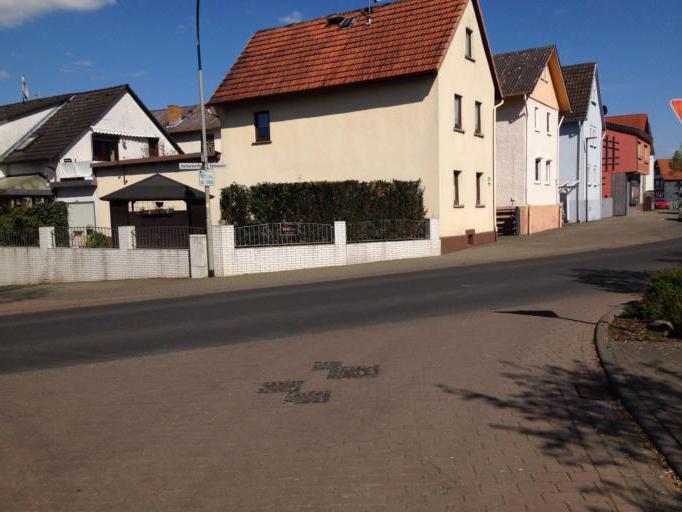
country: DE
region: Hesse
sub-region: Regierungsbezirk Giessen
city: Grunberg
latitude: 50.5597
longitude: 8.9006
